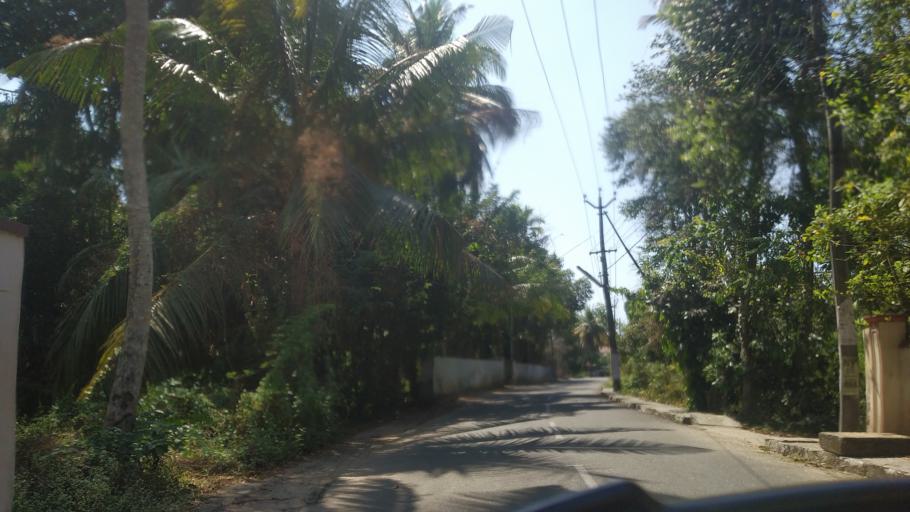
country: IN
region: Kerala
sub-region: Ernakulam
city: Elur
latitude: 10.1319
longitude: 76.2360
